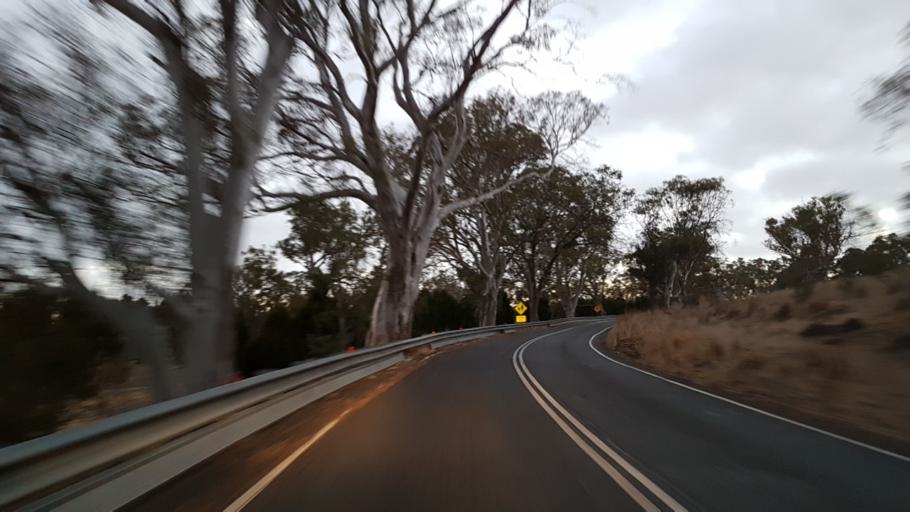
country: AU
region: South Australia
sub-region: Mount Barker
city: Nairne
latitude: -35.0332
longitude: 138.9531
